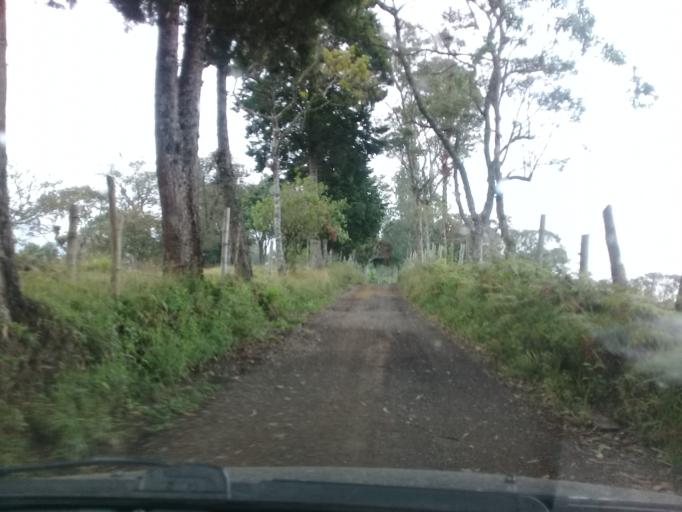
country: CO
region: Cundinamarca
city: Viani
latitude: 4.8345
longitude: -74.5533
